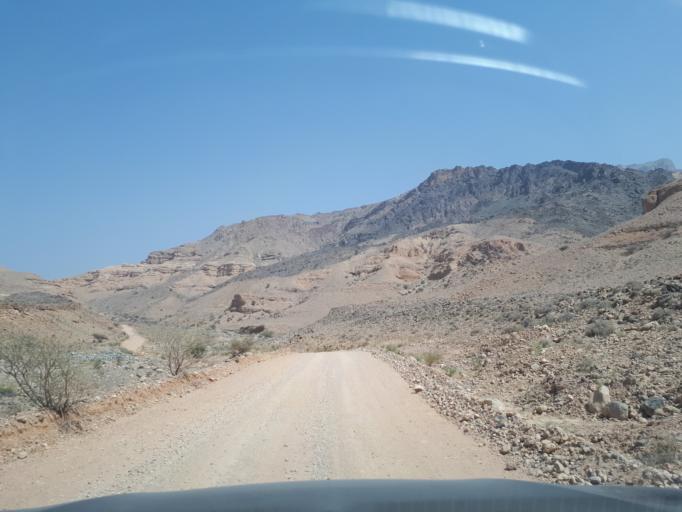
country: OM
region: Ash Sharqiyah
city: Ibra'
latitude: 23.0765
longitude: 58.8749
